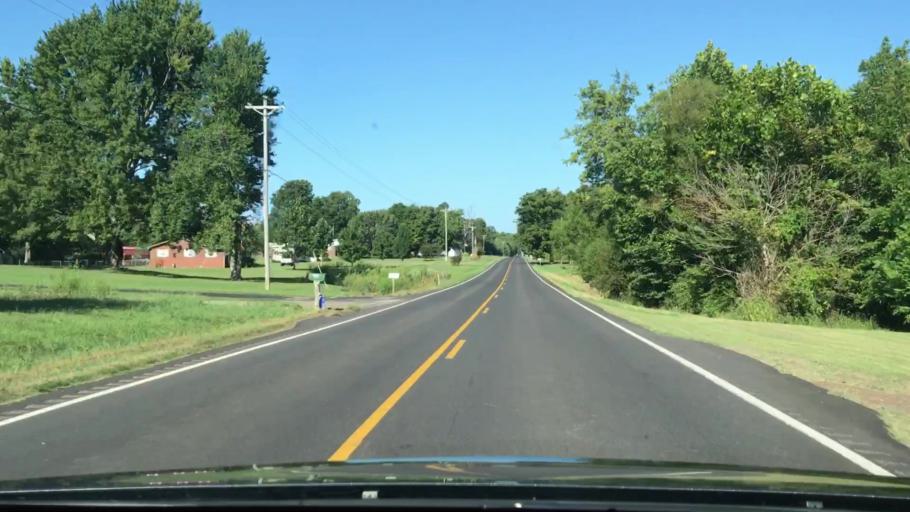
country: US
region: Kentucky
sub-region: Marshall County
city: Benton
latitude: 36.7647
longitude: -88.3349
